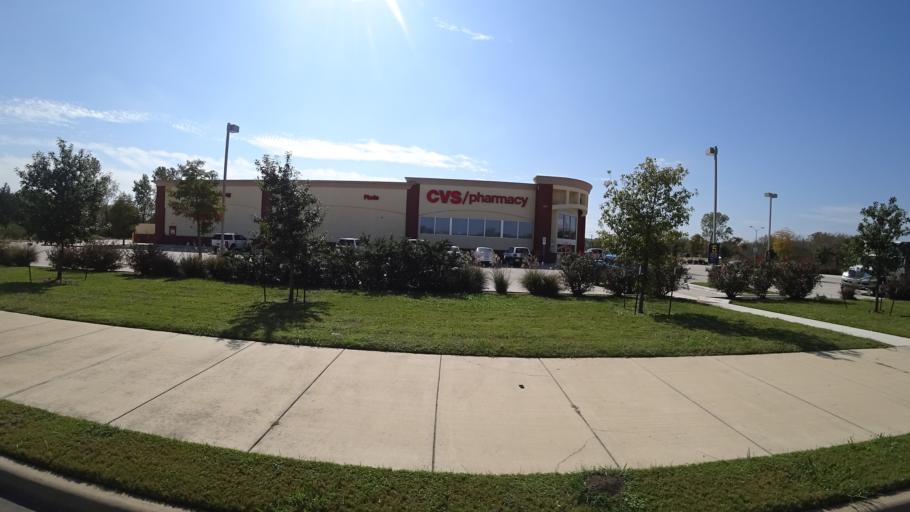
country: US
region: Texas
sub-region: Travis County
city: Pflugerville
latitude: 30.4244
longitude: -97.6258
